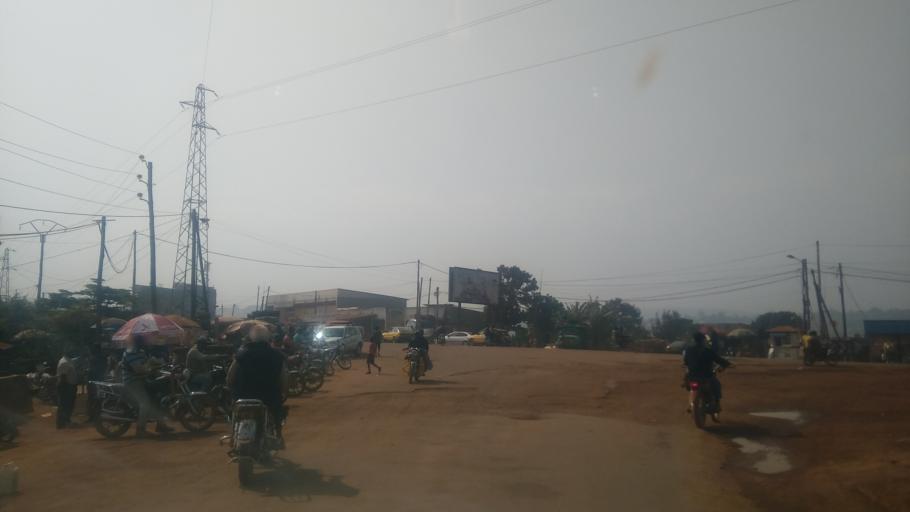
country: CM
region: West
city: Bafoussam
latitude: 5.4975
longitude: 10.3969
